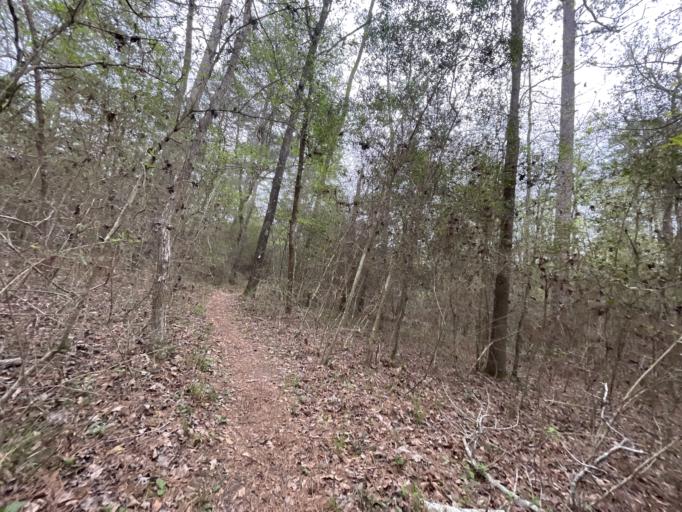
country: US
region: Texas
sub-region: Walker County
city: Huntsville
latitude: 30.6607
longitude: -95.4926
